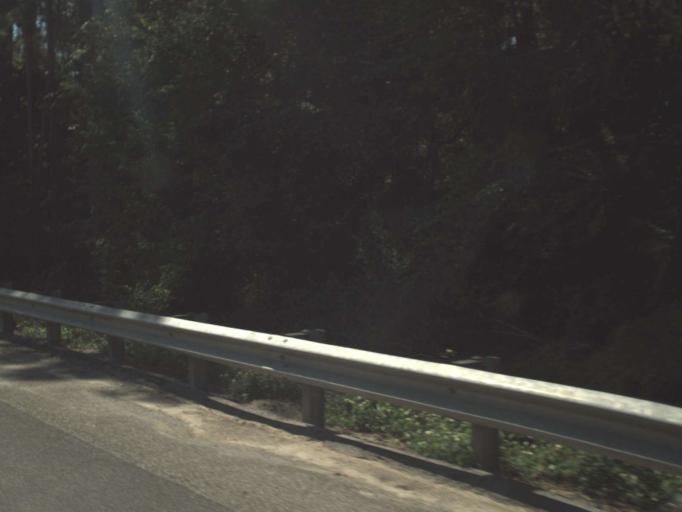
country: US
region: Florida
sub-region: Walton County
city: DeFuniak Springs
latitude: 30.7737
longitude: -86.1139
